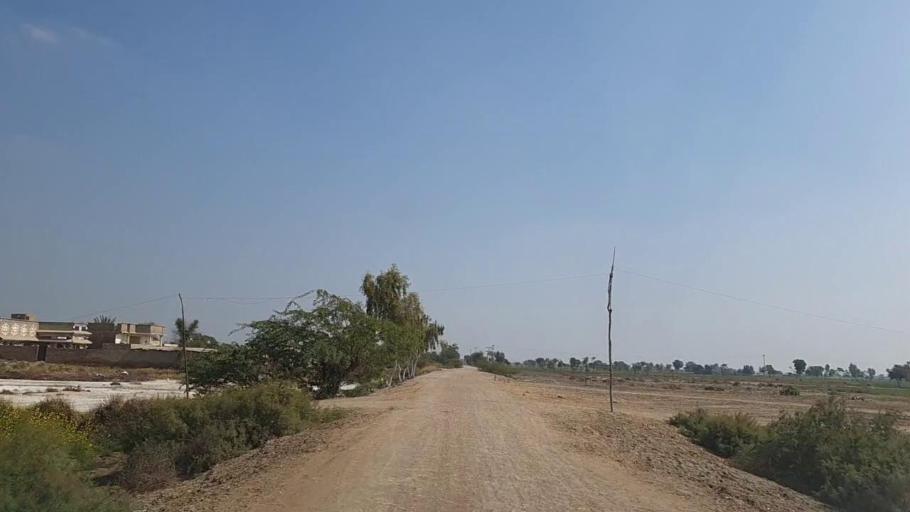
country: PK
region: Sindh
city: Daur
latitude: 26.4530
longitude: 68.2640
